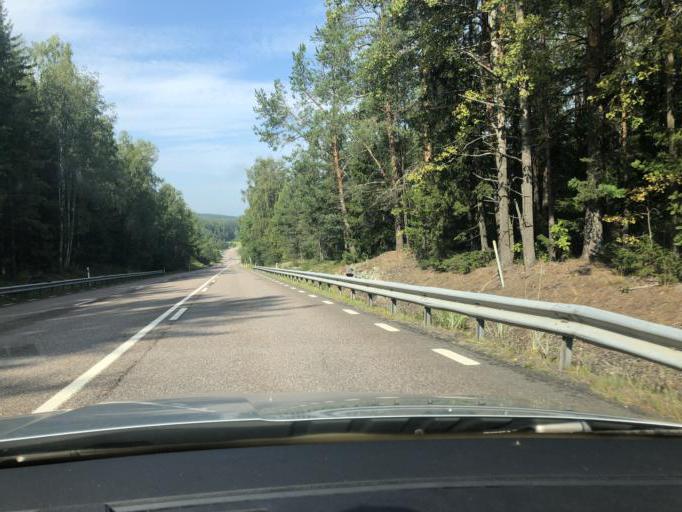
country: SE
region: Vaesternorrland
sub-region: Kramfors Kommun
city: Kramfors
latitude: 62.8153
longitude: 17.8632
